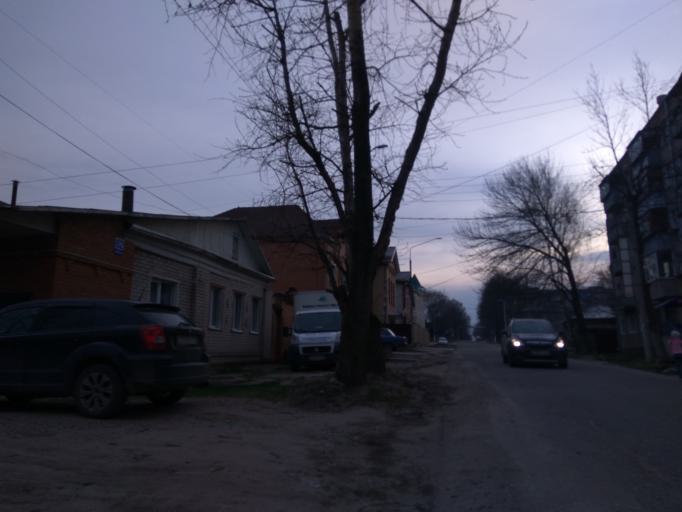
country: RU
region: Vladimir
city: Aleksandrov
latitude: 56.3996
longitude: 38.7305
